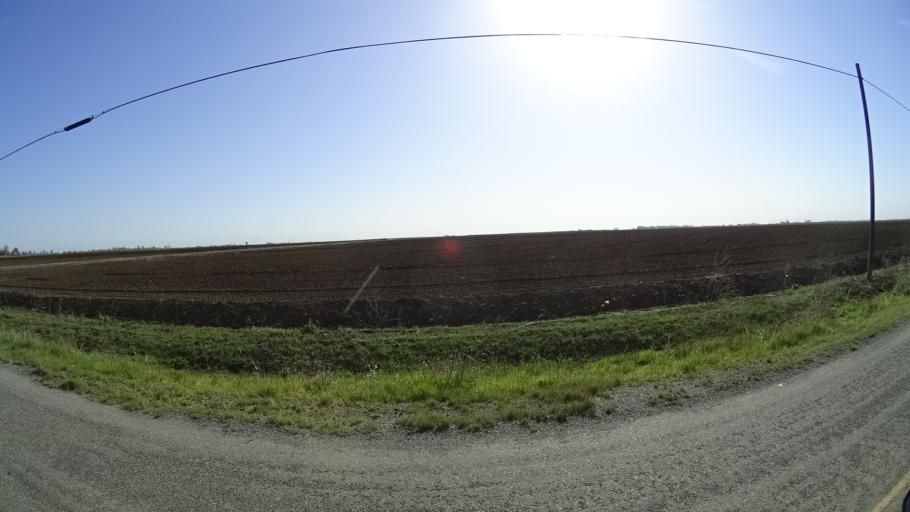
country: US
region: California
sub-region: Glenn County
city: Willows
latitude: 39.5051
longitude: -122.1745
